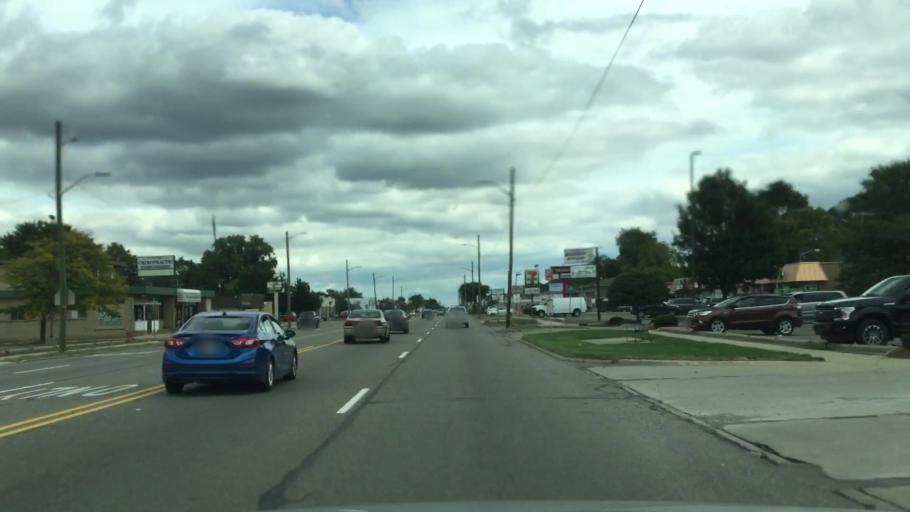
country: US
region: Michigan
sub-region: Wayne County
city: Garden City
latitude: 42.3259
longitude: -83.3208
